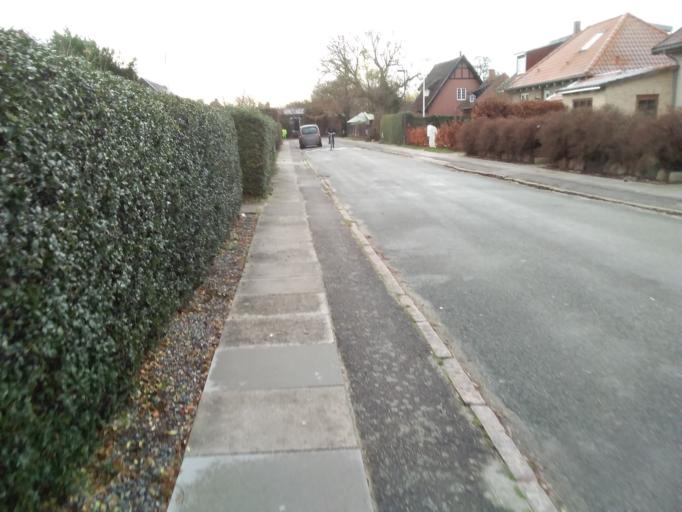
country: DK
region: Capital Region
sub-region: Tarnby Kommune
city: Tarnby
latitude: 55.6407
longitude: 12.6188
